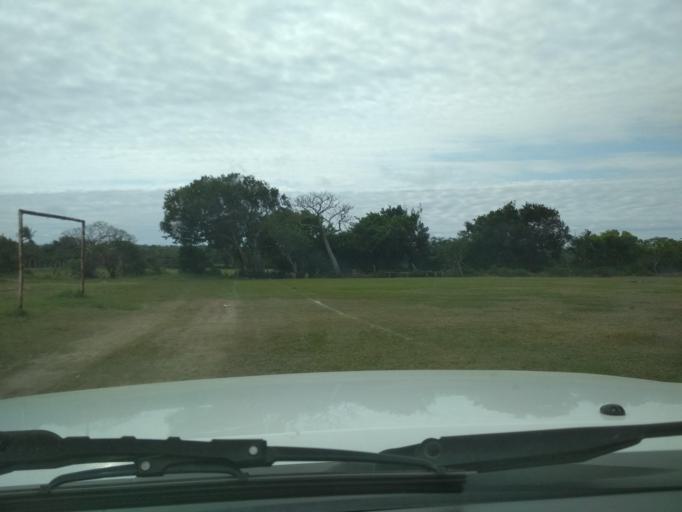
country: MX
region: Veracruz
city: Anton Lizardo
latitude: 19.0358
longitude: -95.9719
